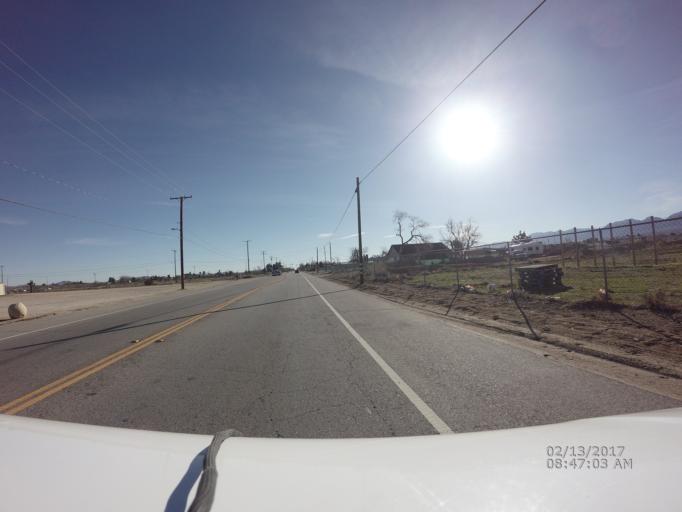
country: US
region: California
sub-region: Los Angeles County
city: Littlerock
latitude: 34.5429
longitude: -117.9779
